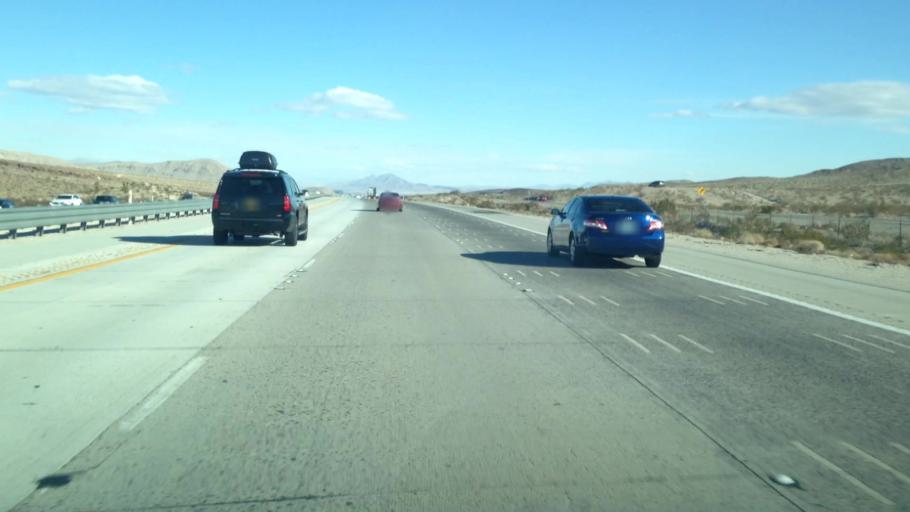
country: US
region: Nevada
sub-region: Clark County
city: Enterprise
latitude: 35.8901
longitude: -115.2212
